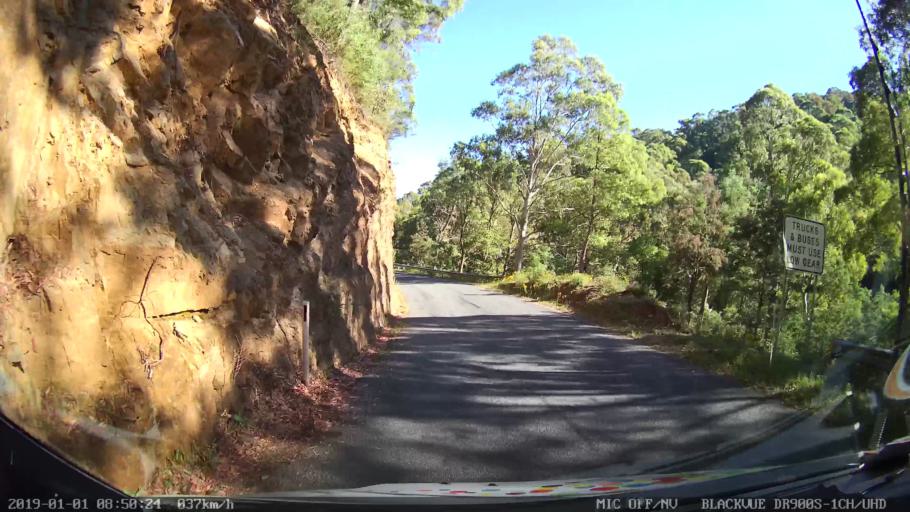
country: AU
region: New South Wales
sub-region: Snowy River
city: Jindabyne
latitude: -36.2766
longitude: 148.2029
